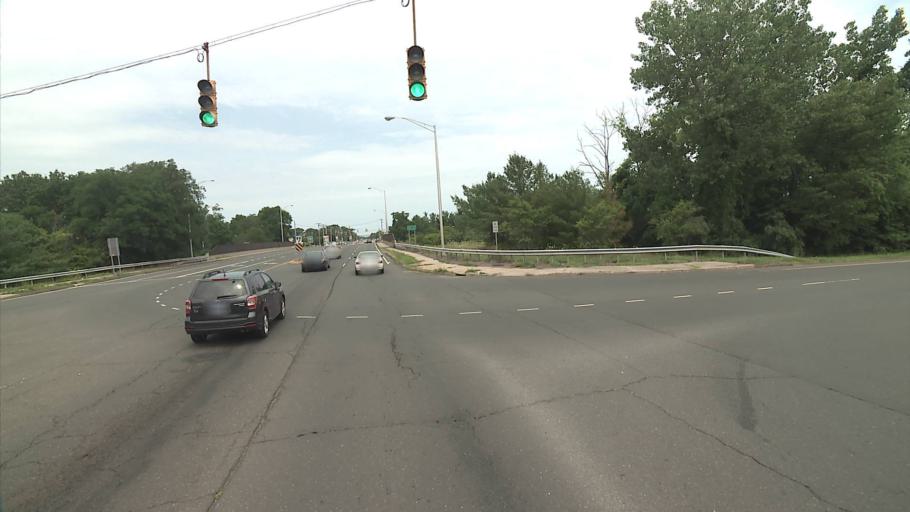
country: US
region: Connecticut
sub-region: Hartford County
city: Newington
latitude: 41.7122
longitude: -72.7650
